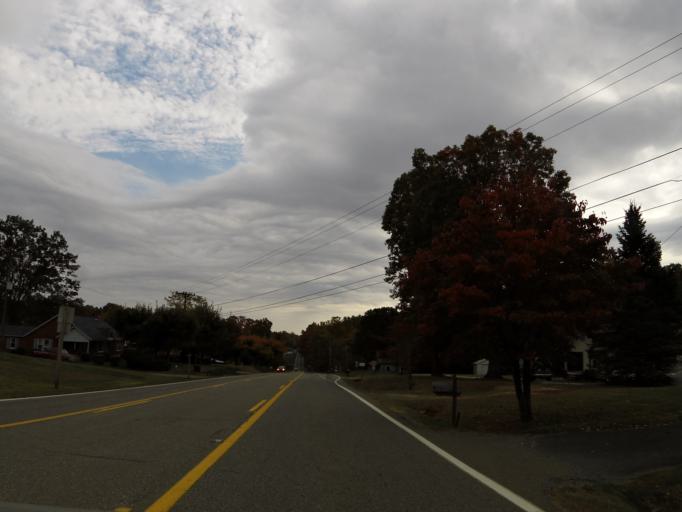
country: US
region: Virginia
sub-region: Carroll County
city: Cana
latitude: 36.6075
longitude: -80.6871
